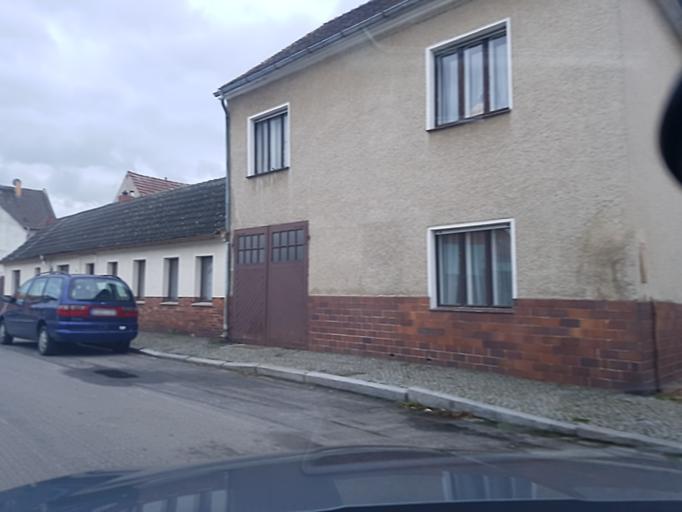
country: DE
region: Brandenburg
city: Doberlug-Kirchhain
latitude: 51.6124
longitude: 13.5485
